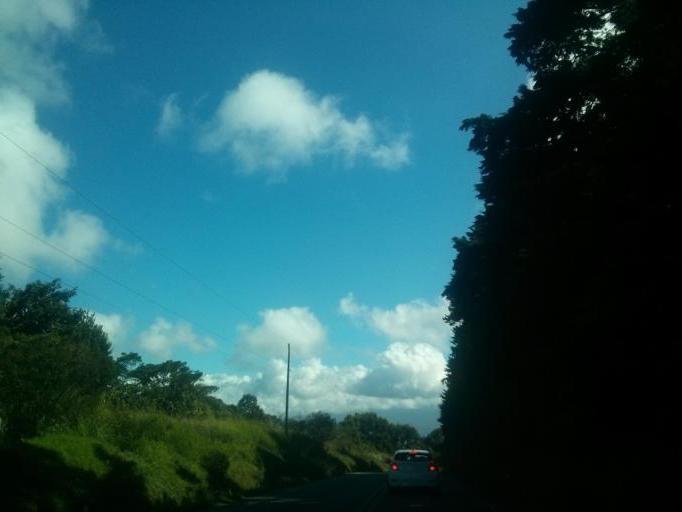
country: CR
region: Cartago
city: Cot
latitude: 9.8869
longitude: -83.8851
